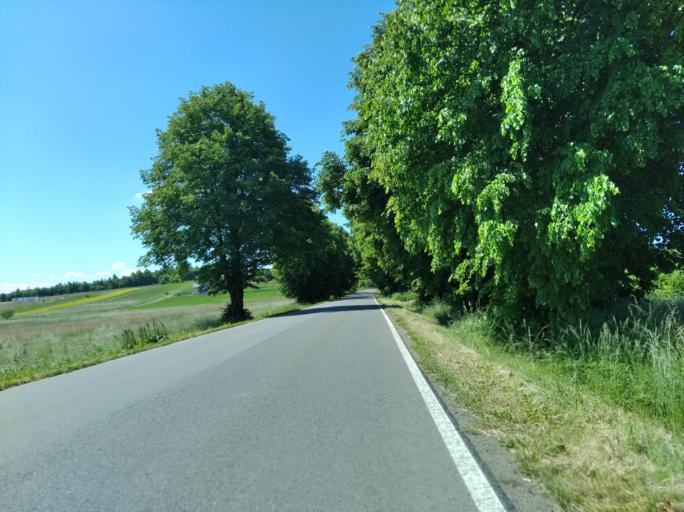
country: PL
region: Subcarpathian Voivodeship
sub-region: Powiat krosnienski
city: Chorkowka
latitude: 49.6548
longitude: 21.6841
